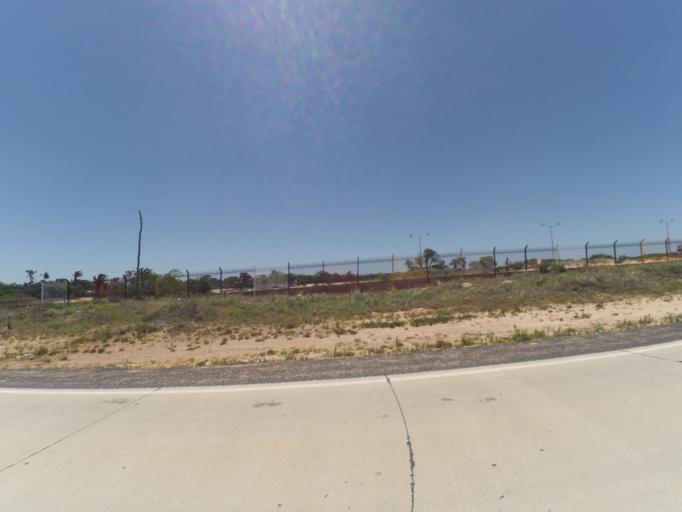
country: BO
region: Santa Cruz
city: Santa Cruz de la Sierra
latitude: -17.8081
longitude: -63.2829
